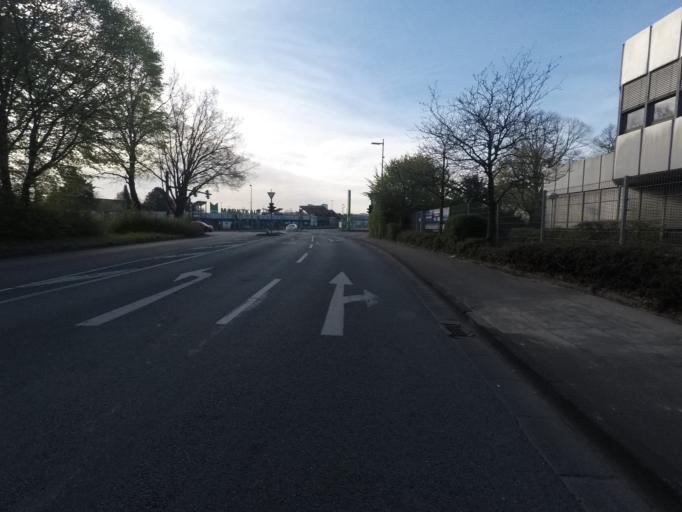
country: DE
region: North Rhine-Westphalia
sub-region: Regierungsbezirk Detmold
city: Bielefeld
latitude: 52.0119
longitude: 8.5937
